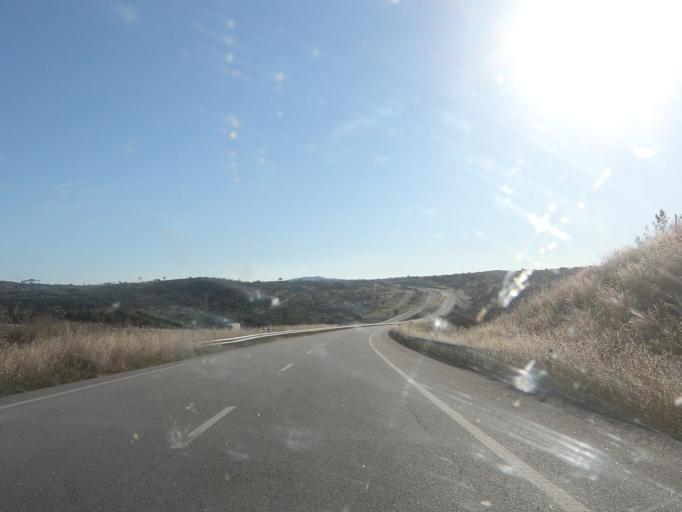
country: PT
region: Guarda
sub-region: Pinhel
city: Pinhel
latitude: 40.6046
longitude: -7.0235
